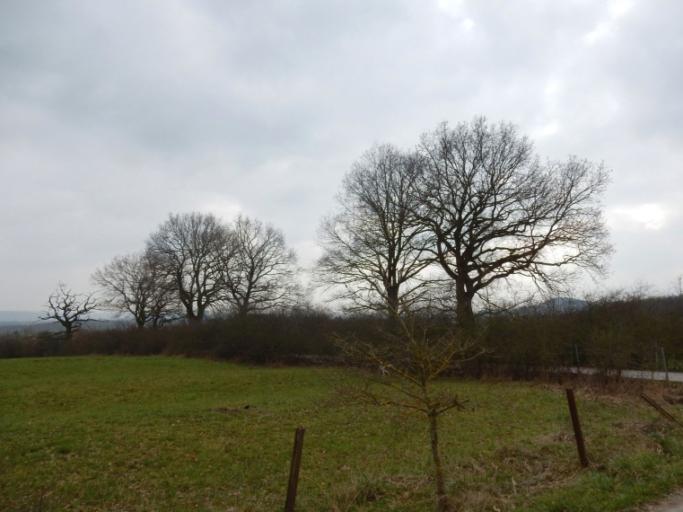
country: LU
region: Luxembourg
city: Soleuvre
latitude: 49.5325
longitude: 5.9578
